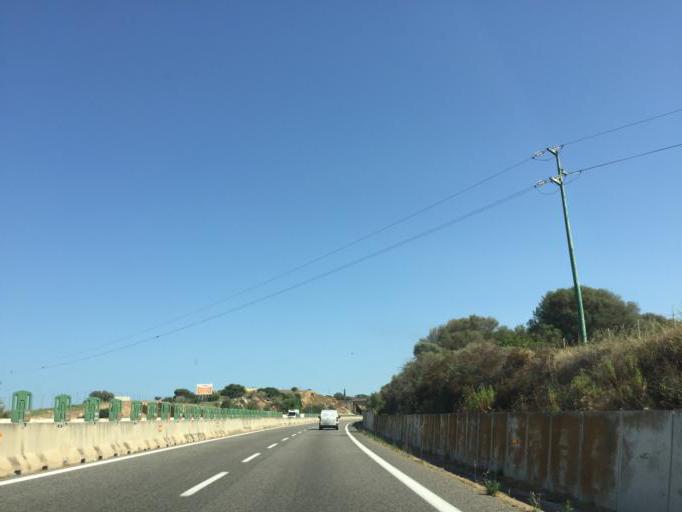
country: IT
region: Sardinia
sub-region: Provincia di Olbia-Tempio
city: Olbia
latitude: 40.8846
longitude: 9.4962
